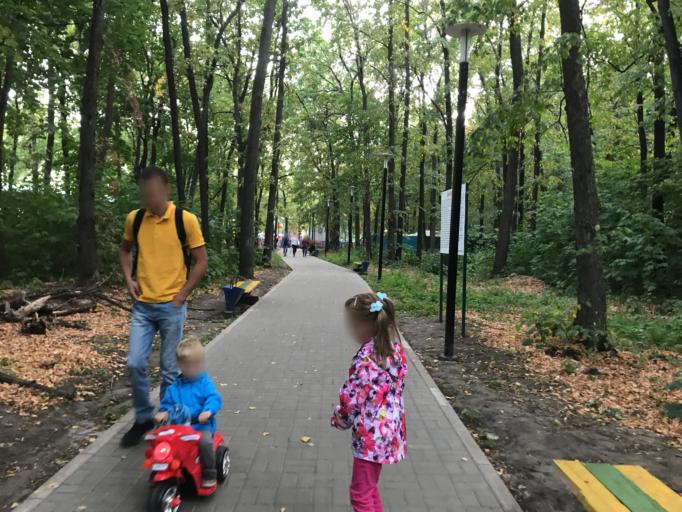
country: RU
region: Ulyanovsk
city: Mirnyy
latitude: 54.3939
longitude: 48.5780
